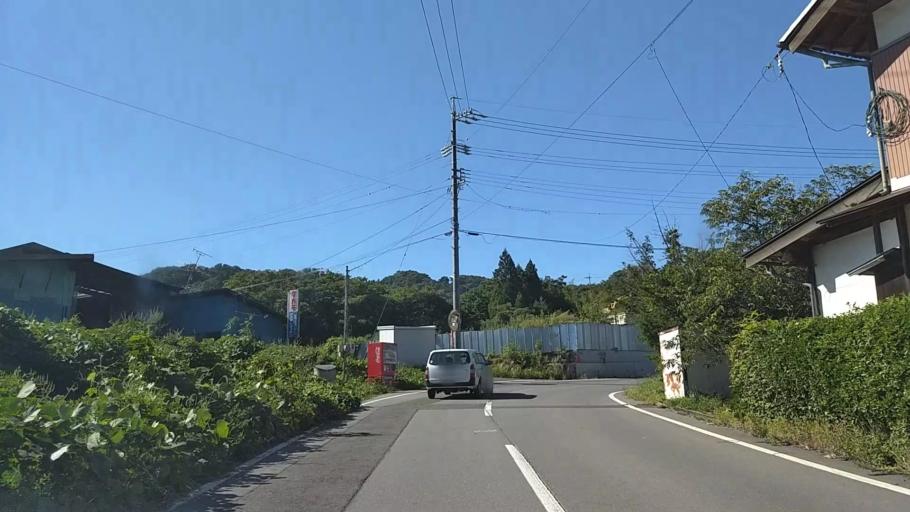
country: JP
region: Nagano
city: Nagano-shi
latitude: 36.5778
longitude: 138.1137
